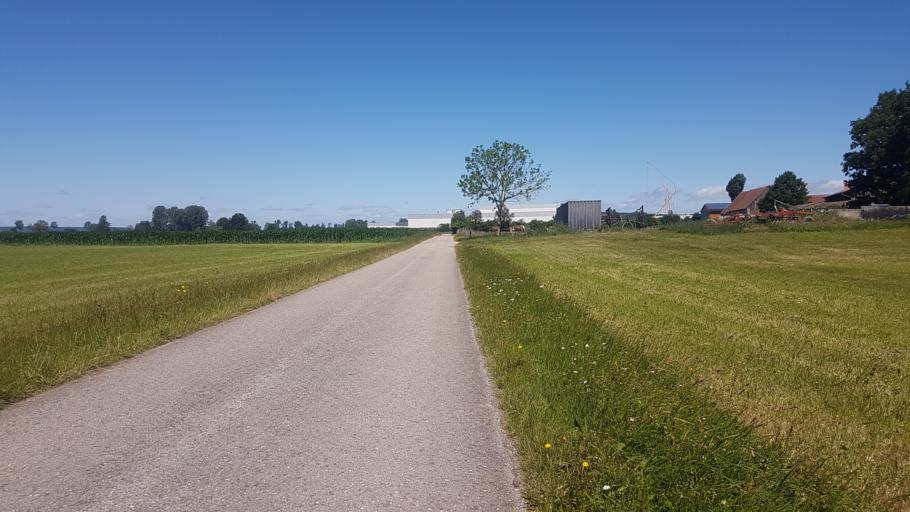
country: DE
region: Bavaria
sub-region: Regierungsbezirk Mittelfranken
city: Herrieden
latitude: 49.2236
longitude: 10.5144
